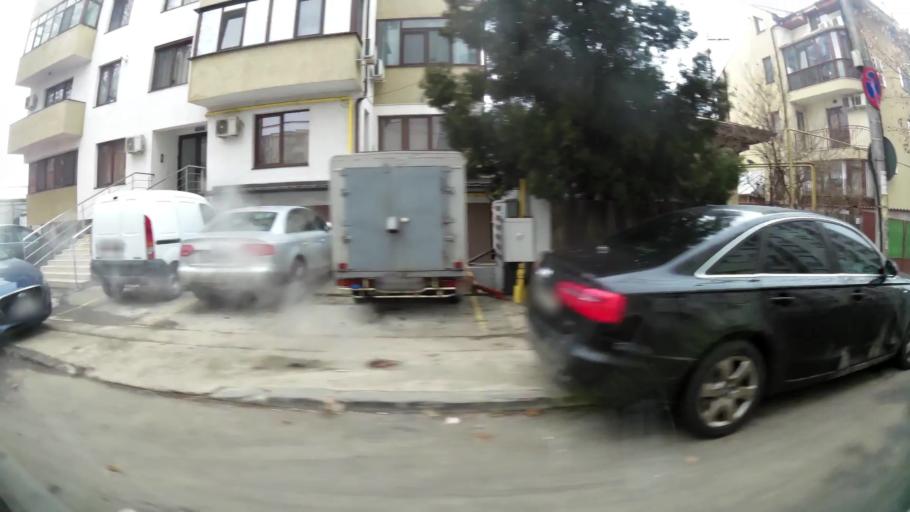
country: RO
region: Ilfov
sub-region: Comuna Chiajna
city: Rosu
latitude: 44.4435
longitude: 26.0327
